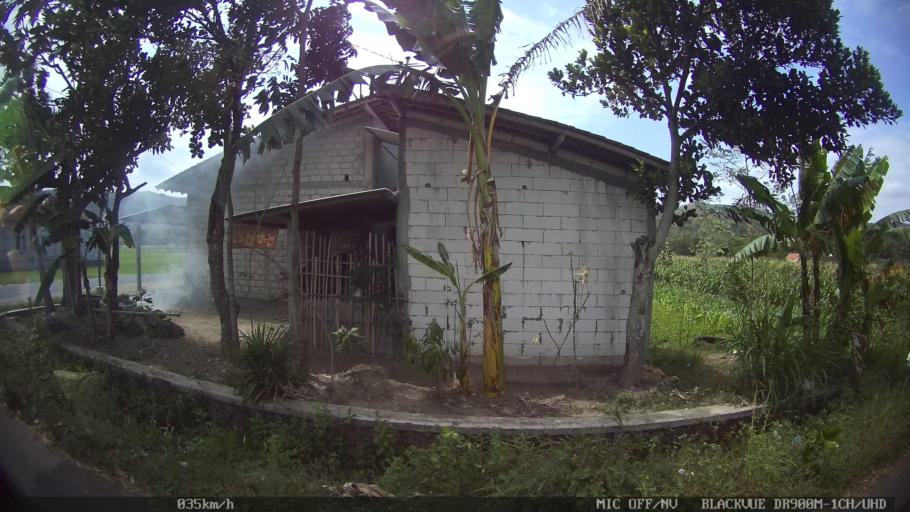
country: ID
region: Central Java
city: Candi Prambanan
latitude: -7.8106
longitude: 110.5003
